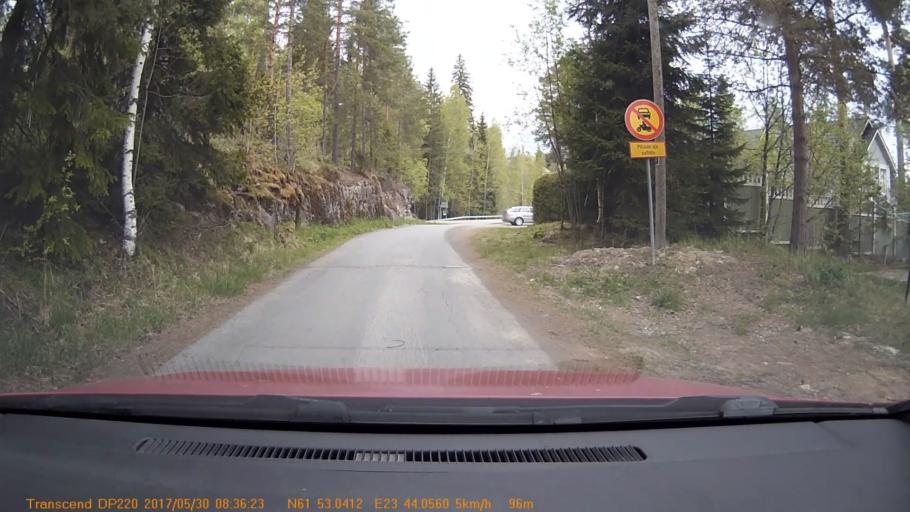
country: FI
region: Pirkanmaa
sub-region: Tampere
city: Kuru
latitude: 61.8842
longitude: 23.7343
